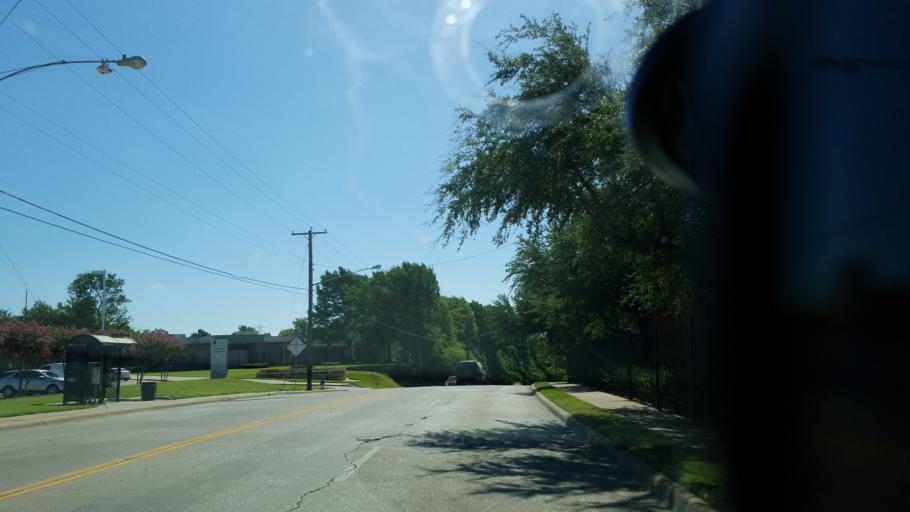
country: US
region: Texas
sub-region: Dallas County
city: Cockrell Hill
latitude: 32.7010
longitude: -96.8213
